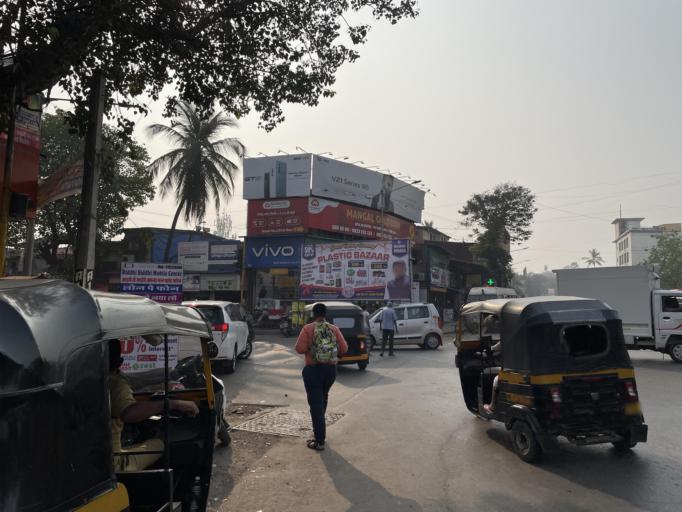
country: IN
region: Maharashtra
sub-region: Mumbai Suburban
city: Borivli
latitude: 19.1959
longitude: 72.8222
